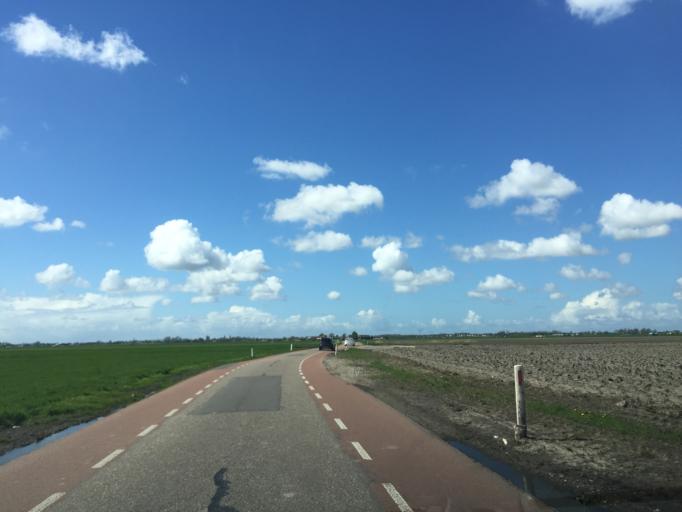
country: NL
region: South Holland
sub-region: Gemeente Kaag en Braassem
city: Leimuiden
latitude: 52.2047
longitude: 4.7091
